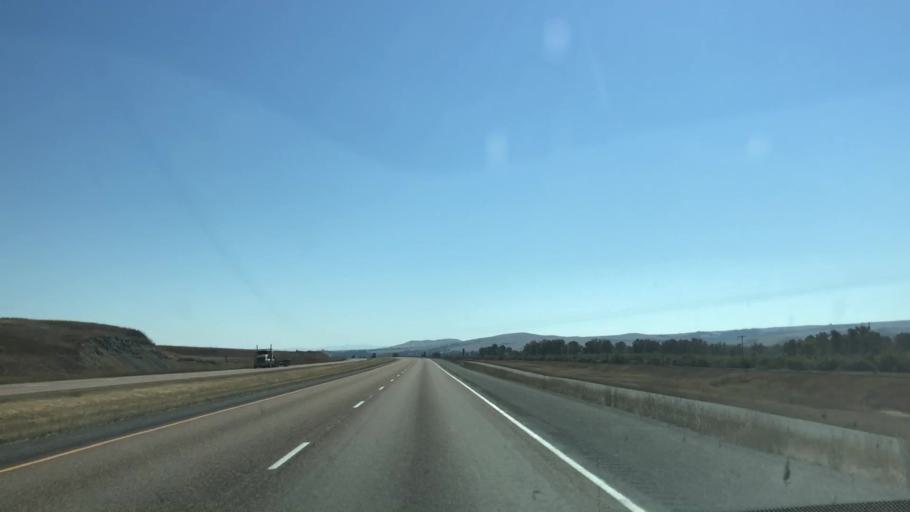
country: US
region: Montana
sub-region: Granite County
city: Philipsburg
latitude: 46.6218
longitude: -113.0649
